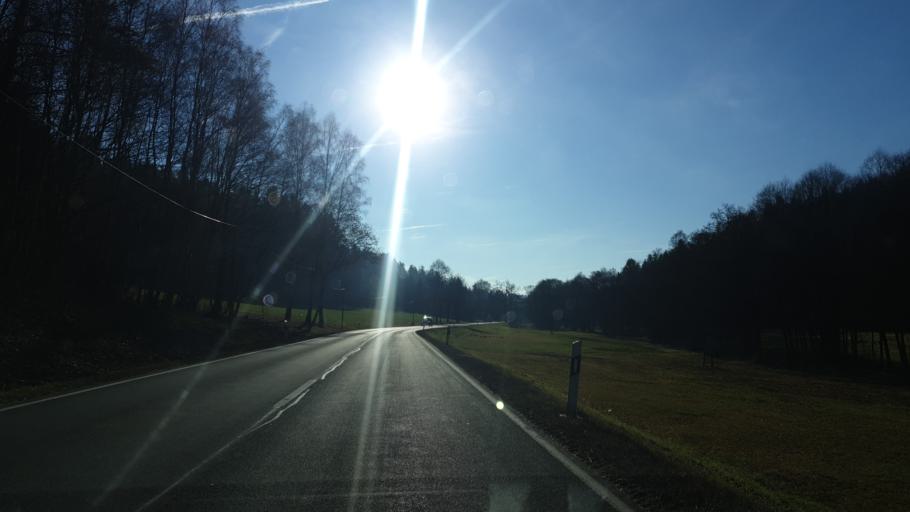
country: DE
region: Saxony
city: Bad Brambach
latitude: 50.2648
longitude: 12.3010
